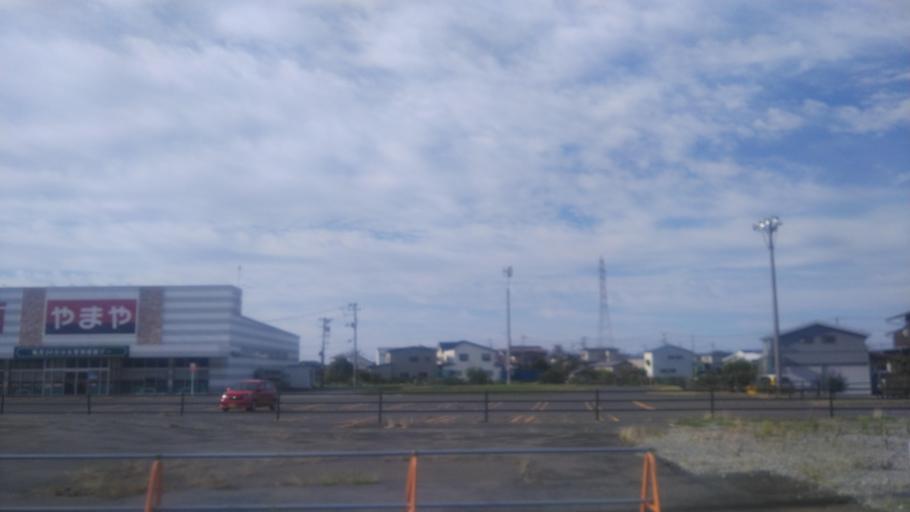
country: JP
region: Akita
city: Noshiromachi
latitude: 40.1887
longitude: 140.0404
